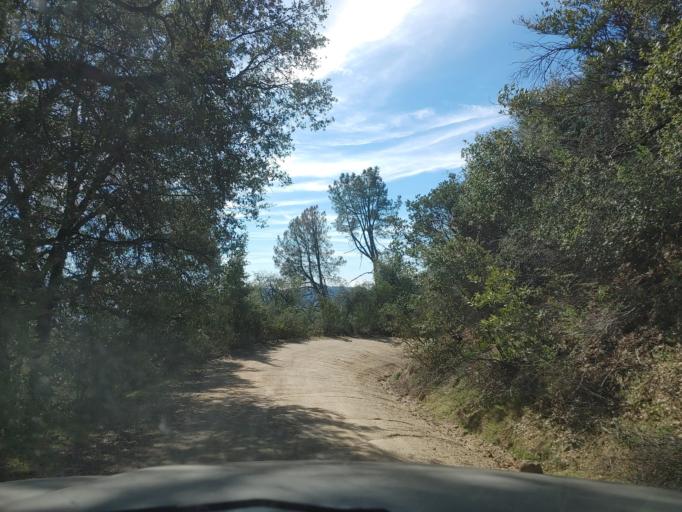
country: US
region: California
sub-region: Madera County
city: Ahwahnee
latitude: 37.4154
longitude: -119.6968
